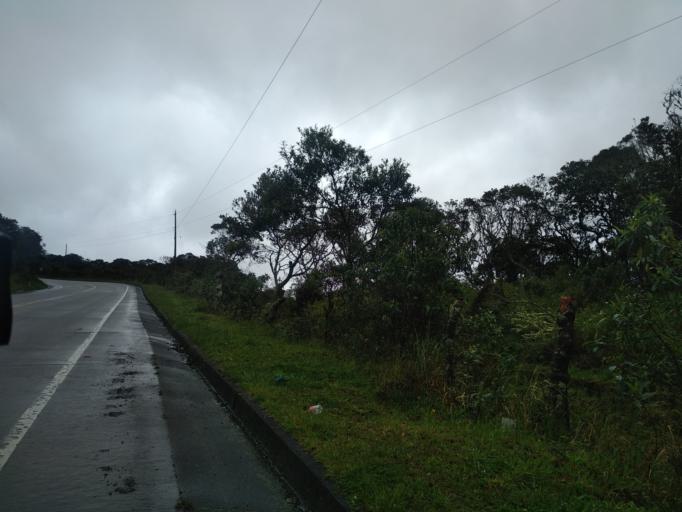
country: EC
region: Loja
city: Catamayo
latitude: -3.8621
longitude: -79.2821
